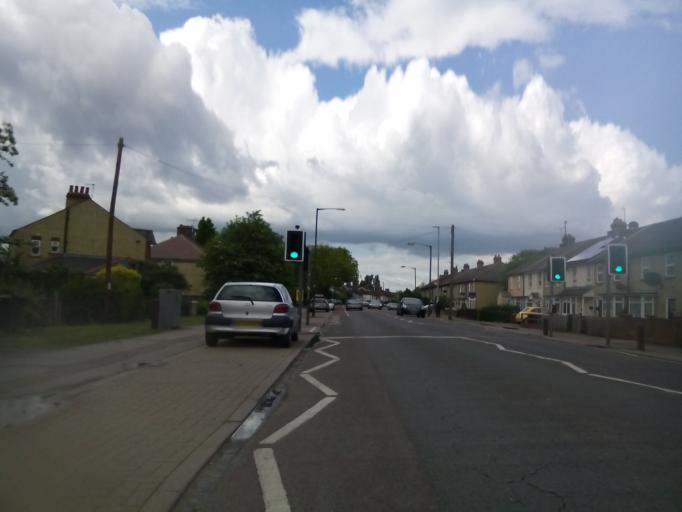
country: GB
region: England
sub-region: Cambridgeshire
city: Cambridge
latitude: 52.2030
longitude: 0.1527
